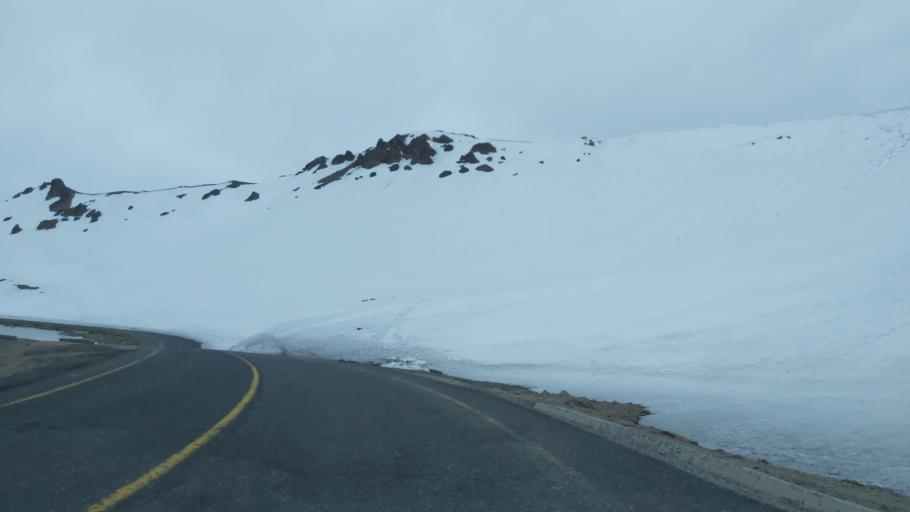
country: CL
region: Maule
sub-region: Provincia de Linares
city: Colbun
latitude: -36.0139
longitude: -70.5063
